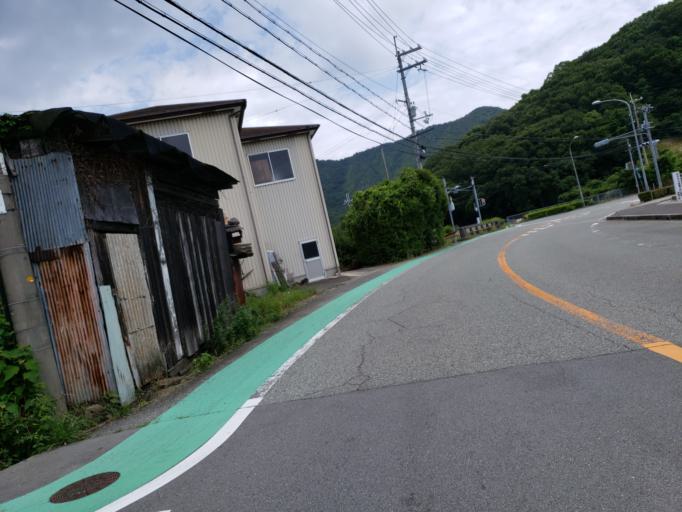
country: JP
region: Hyogo
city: Aioi
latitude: 34.7868
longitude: 134.4791
